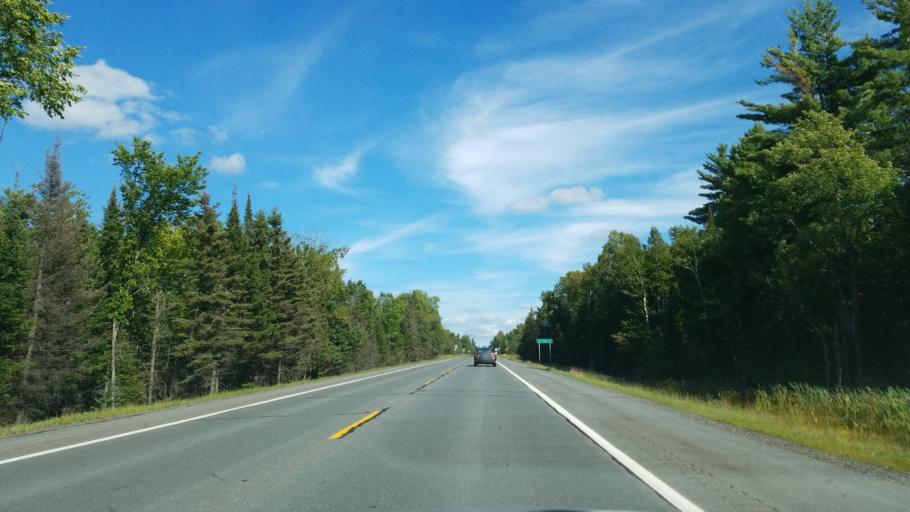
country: US
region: Michigan
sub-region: Baraga County
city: L'Anse
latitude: 46.5788
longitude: -88.4008
